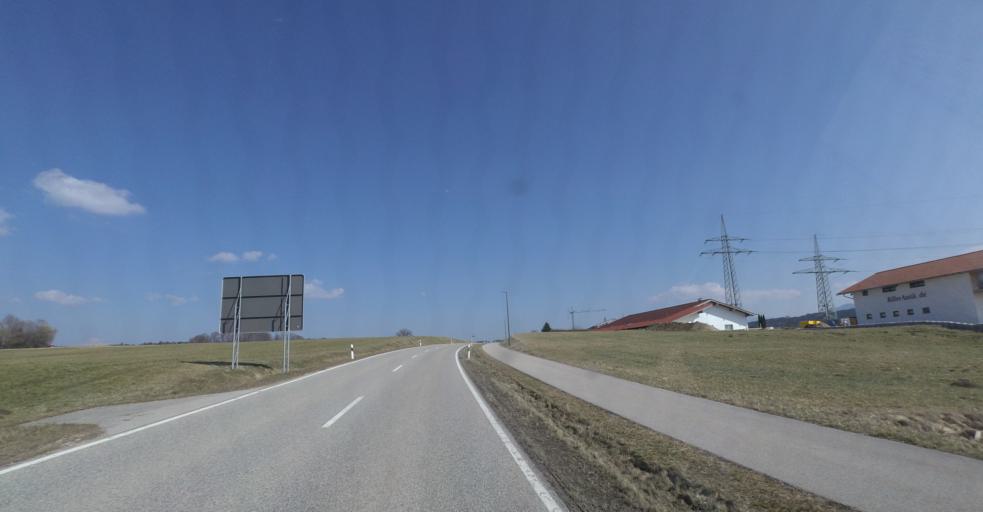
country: DE
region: Bavaria
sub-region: Upper Bavaria
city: Grabenstatt
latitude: 47.8515
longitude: 12.5440
